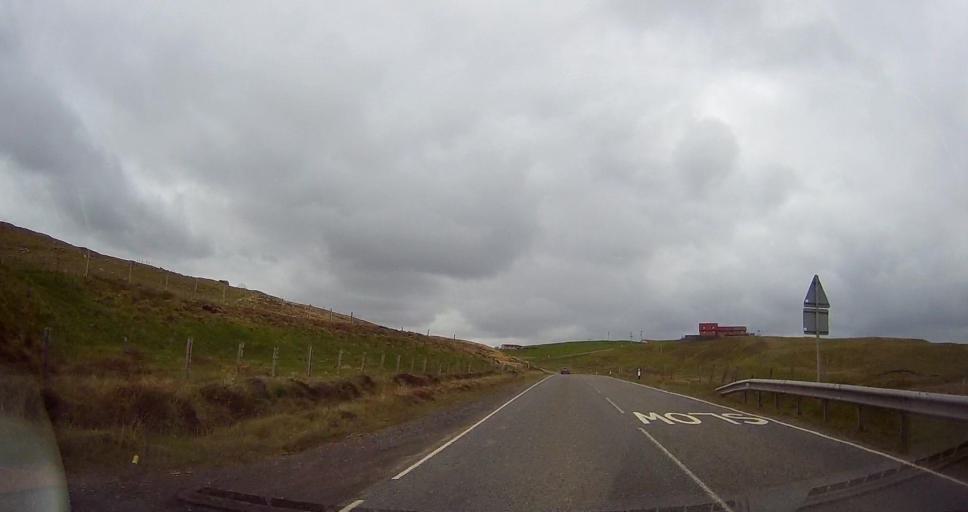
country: GB
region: Scotland
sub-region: Shetland Islands
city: Lerwick
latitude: 60.3843
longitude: -1.3422
